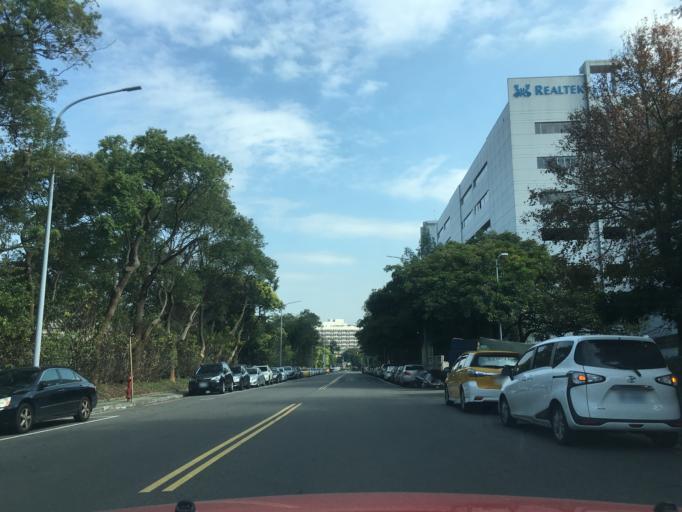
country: TW
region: Taiwan
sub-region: Hsinchu
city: Hsinchu
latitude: 24.7801
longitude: 120.9937
